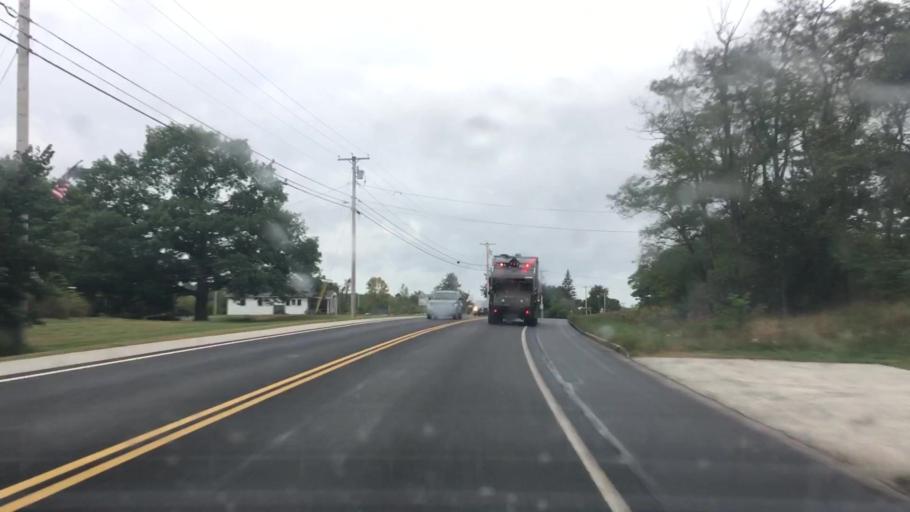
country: US
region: Maine
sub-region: Penobscot County
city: Orrington
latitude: 44.7461
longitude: -68.8078
